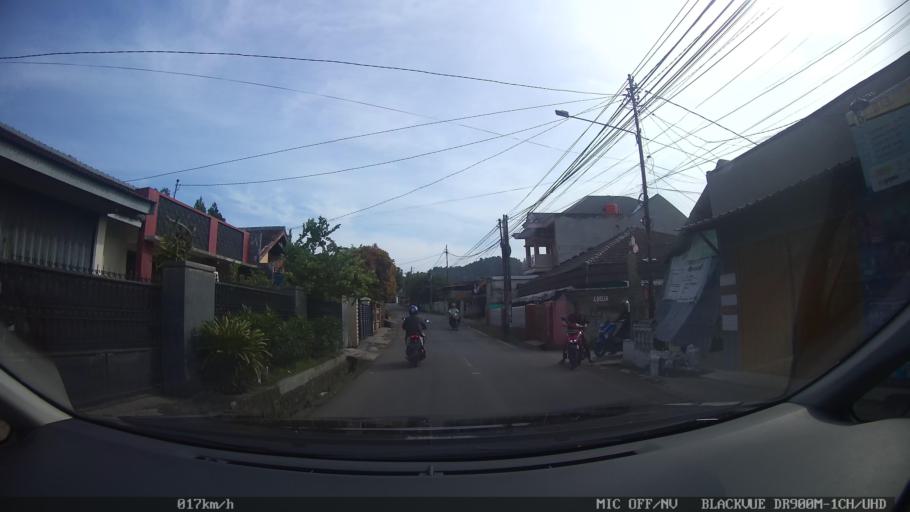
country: ID
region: Lampung
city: Kedaton
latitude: -5.3964
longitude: 105.2658
